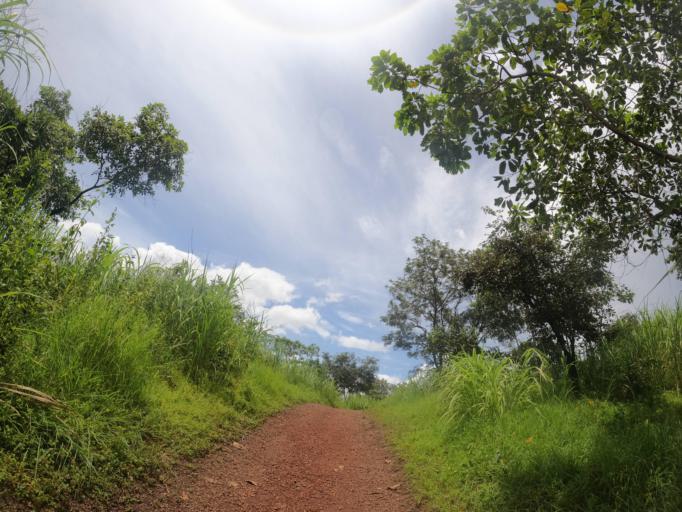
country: SL
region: Northern Province
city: Binkolo
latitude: 9.1604
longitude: -12.1877
